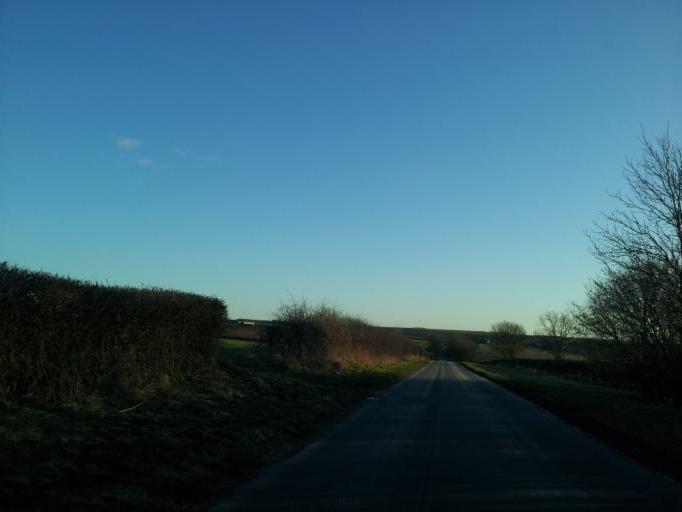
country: GB
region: England
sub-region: Lincolnshire
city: Horncastle
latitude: 53.2560
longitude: -0.1057
